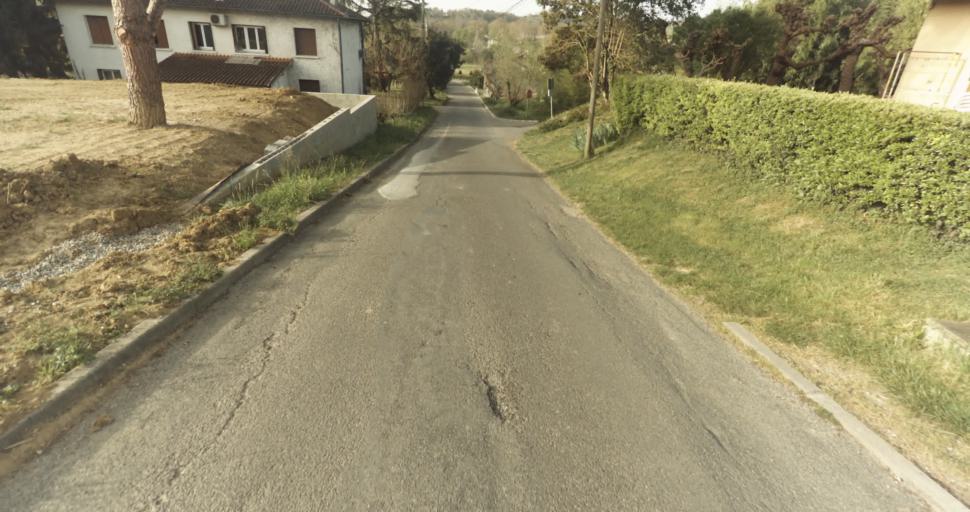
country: FR
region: Midi-Pyrenees
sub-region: Departement du Tarn-et-Garonne
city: Moissac
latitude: 44.1208
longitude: 1.1074
